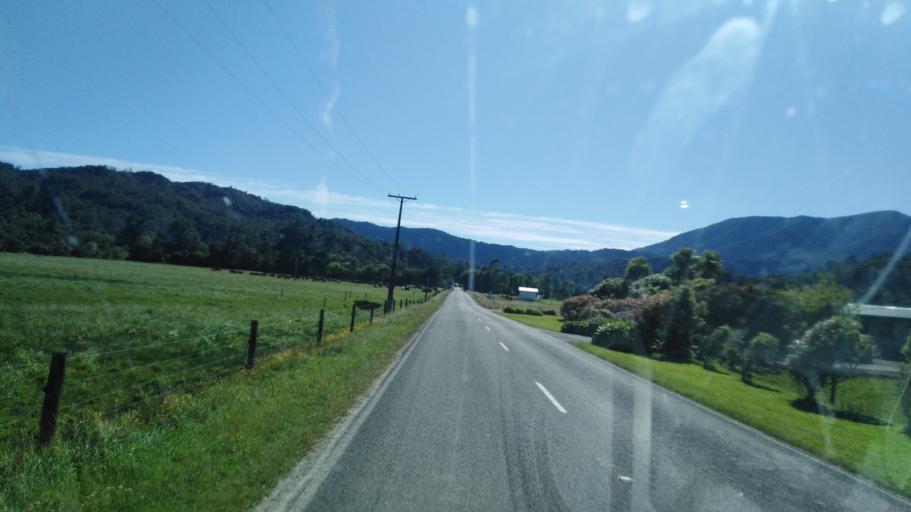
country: NZ
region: West Coast
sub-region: Buller District
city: Westport
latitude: -41.5337
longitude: 171.9606
